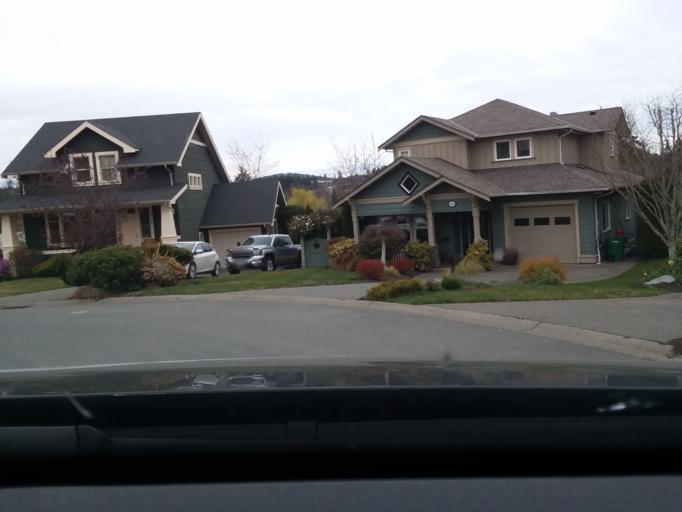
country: CA
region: British Columbia
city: Victoria
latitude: 48.4805
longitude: -123.4166
